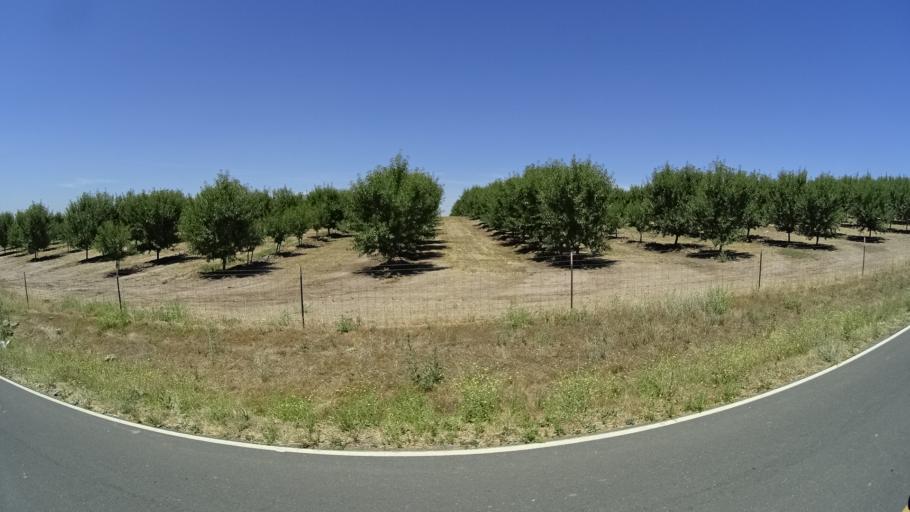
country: US
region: California
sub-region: Calaveras County
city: Rancho Calaveras
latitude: 38.1071
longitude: -120.9448
